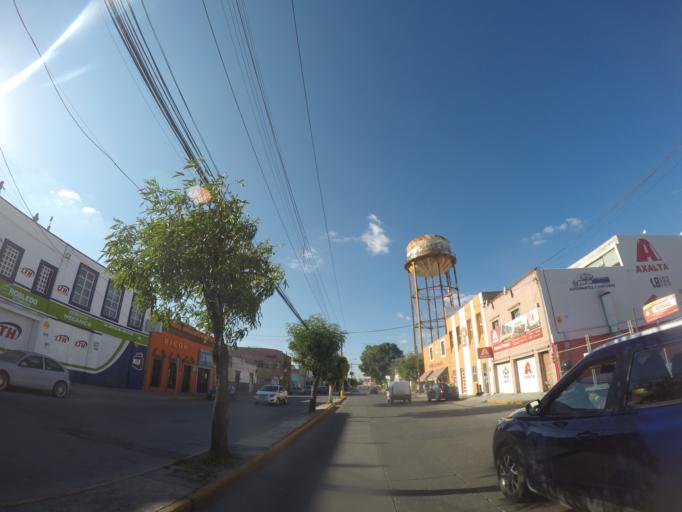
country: MX
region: San Luis Potosi
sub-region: San Luis Potosi
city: San Luis Potosi
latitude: 22.1623
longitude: -100.9801
